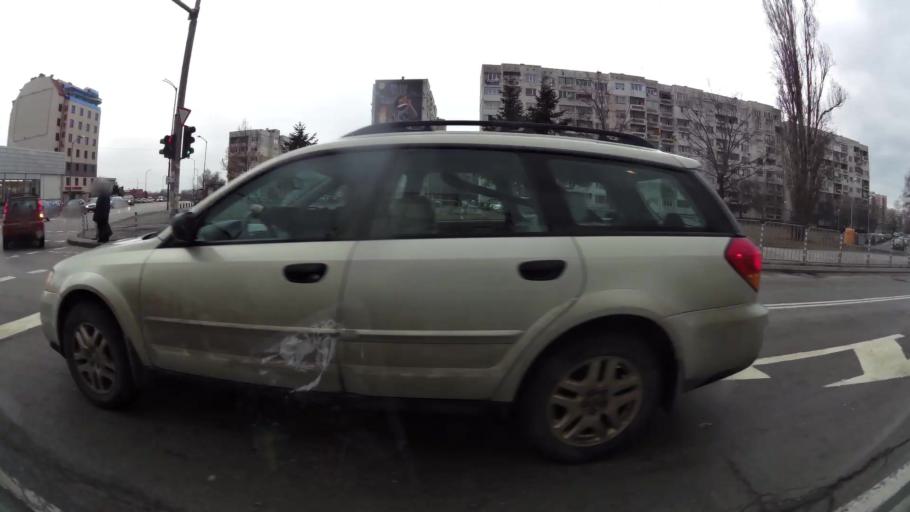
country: BG
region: Sofia-Capital
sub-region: Stolichna Obshtina
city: Sofia
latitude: 42.7317
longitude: 23.2865
